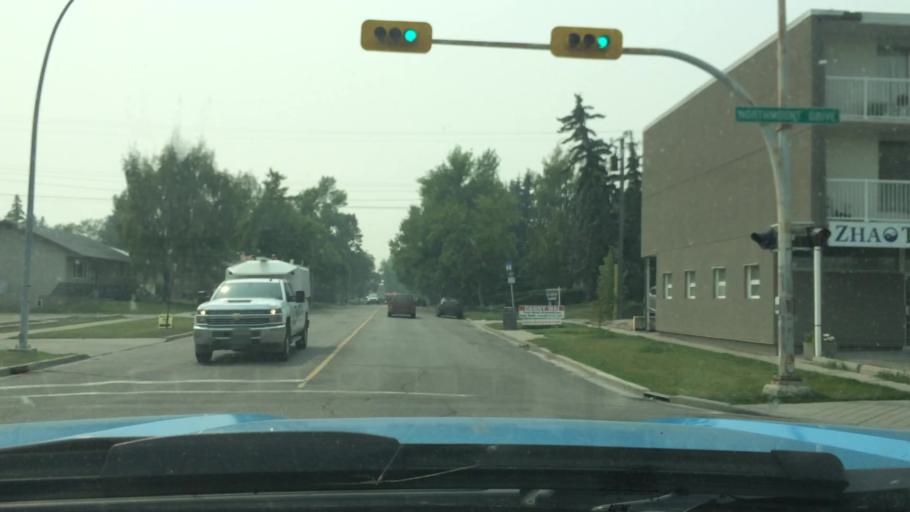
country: CA
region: Alberta
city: Calgary
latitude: 51.0931
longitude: -114.1289
